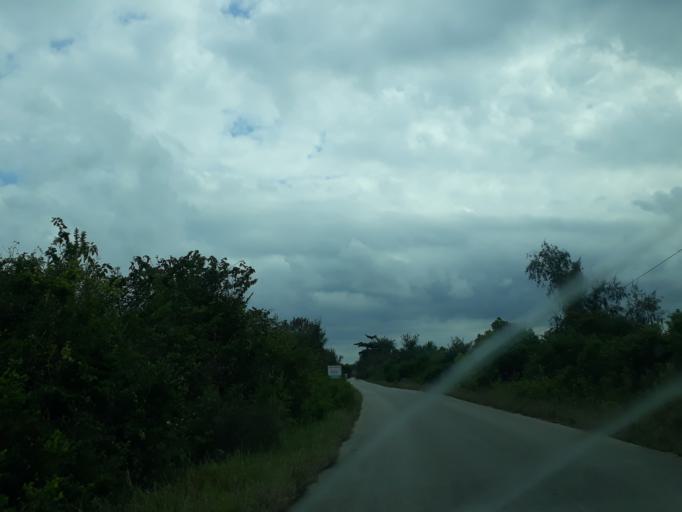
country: TZ
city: Kiwengwa
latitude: -6.0858
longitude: 39.4245
